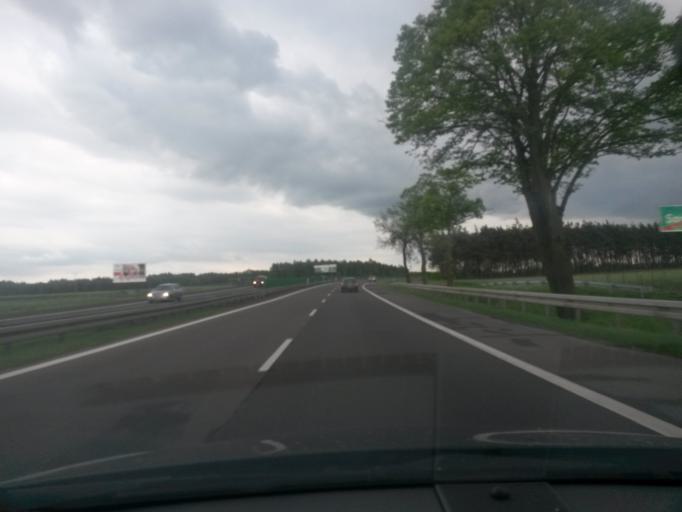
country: PL
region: Masovian Voivodeship
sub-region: Powiat plonski
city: Zaluski
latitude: 52.5792
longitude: 20.4763
